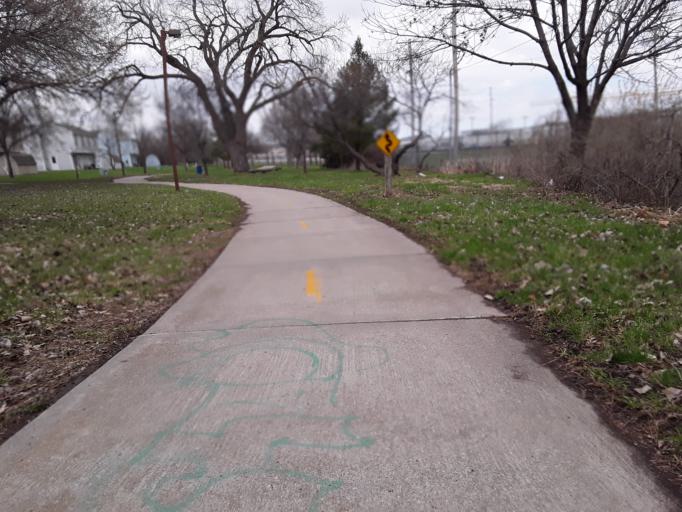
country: US
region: Nebraska
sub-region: Lancaster County
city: Lincoln
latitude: 40.8315
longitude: -96.6864
